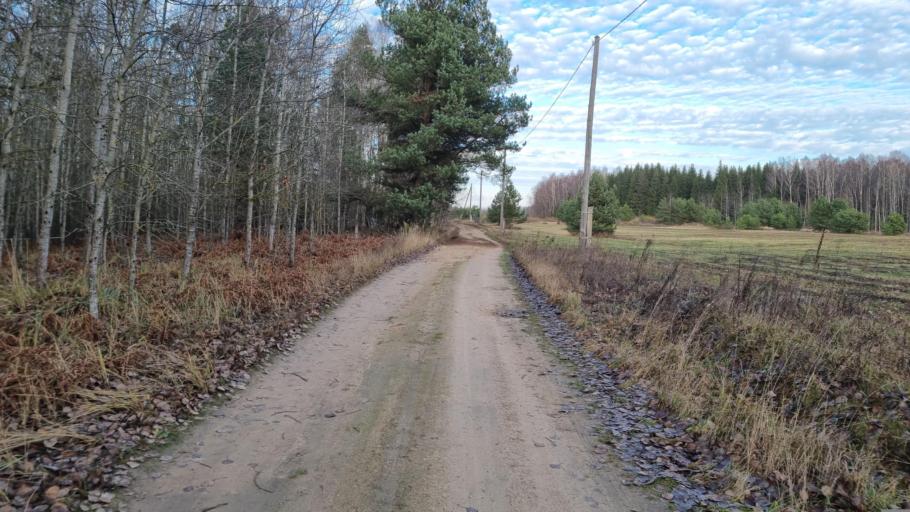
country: LV
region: Kekava
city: Kekava
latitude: 56.7832
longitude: 24.2471
